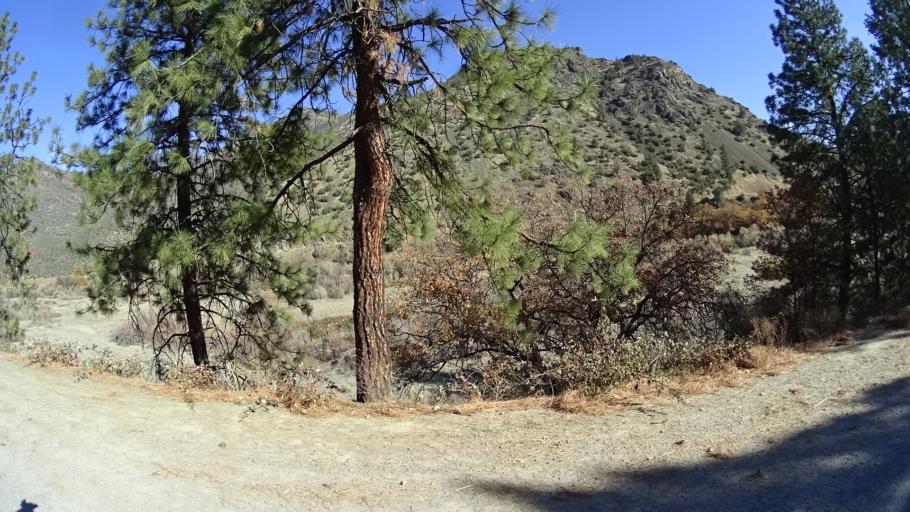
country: US
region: California
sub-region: Siskiyou County
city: Yreka
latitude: 41.8357
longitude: -122.6693
